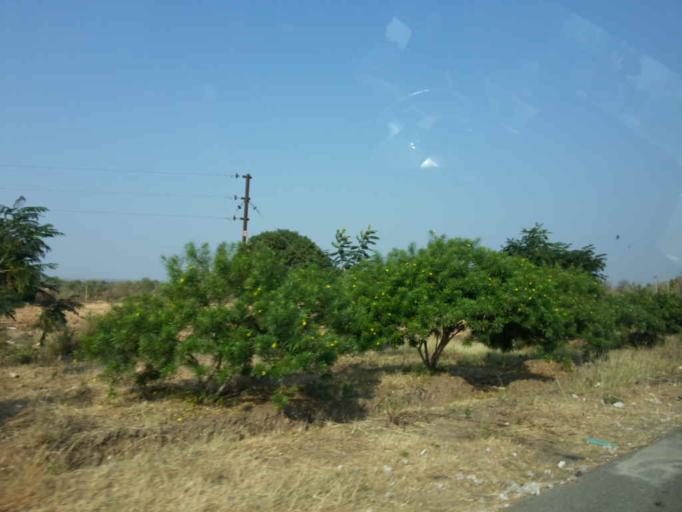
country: IN
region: Telangana
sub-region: Nizamabad District
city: Kamareddi
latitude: 18.4748
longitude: 78.2218
